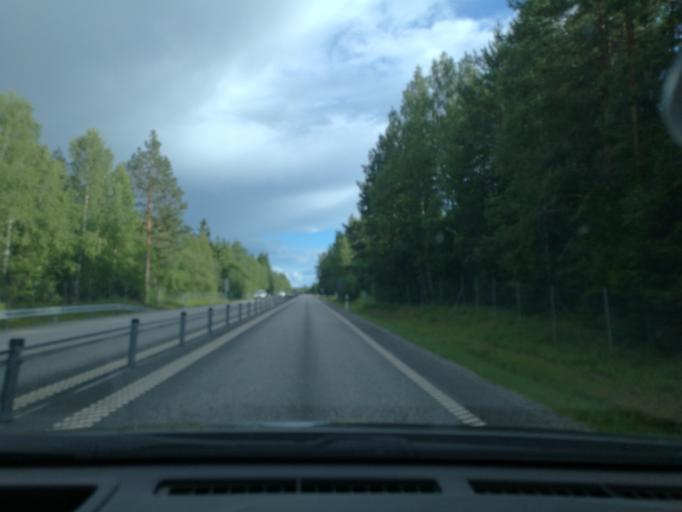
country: SE
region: Vaestmanland
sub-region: Surahammars Kommun
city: Surahammar
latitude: 59.7399
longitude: 16.2276
